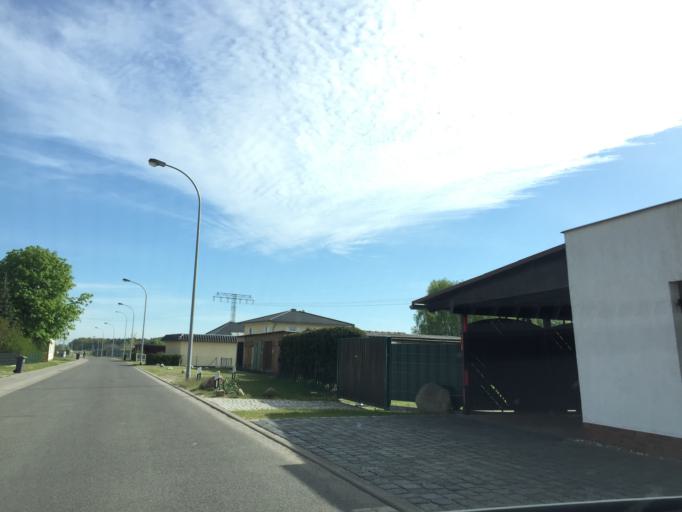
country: DE
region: Mecklenburg-Vorpommern
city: Torgelow
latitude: 53.6374
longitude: 14.0237
